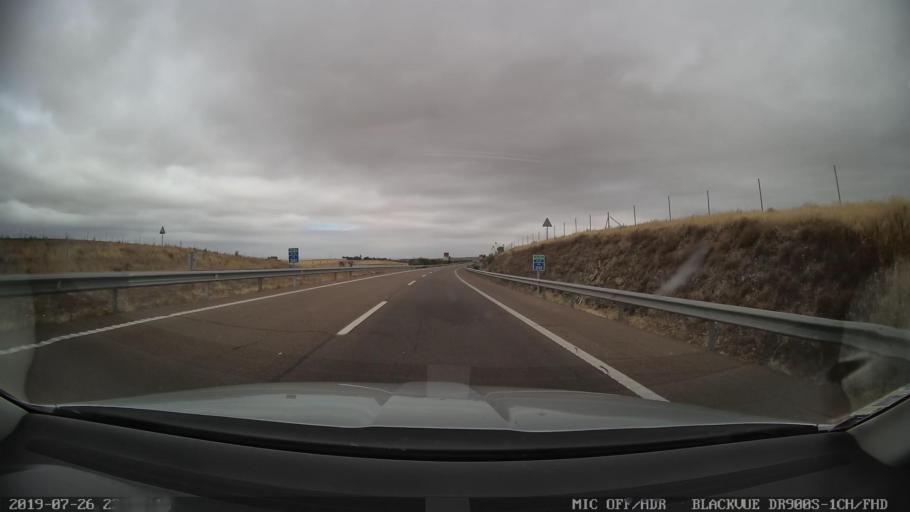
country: ES
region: Extremadura
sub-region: Provincia de Caceres
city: Trujillo
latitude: 39.3912
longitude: -5.8869
